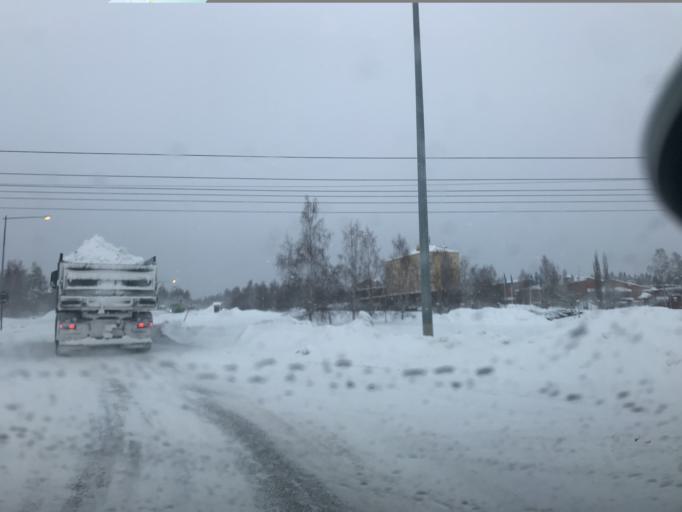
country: SE
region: Norrbotten
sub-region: Lulea Kommun
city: Lulea
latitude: 65.6153
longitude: 22.1326
